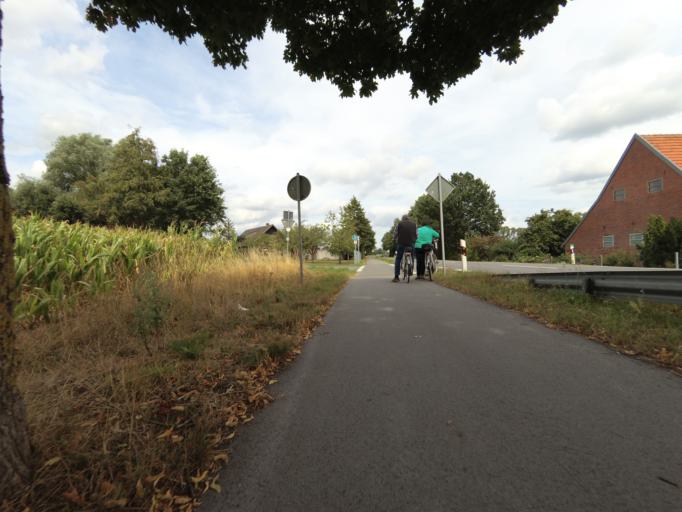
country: DE
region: North Rhine-Westphalia
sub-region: Regierungsbezirk Munster
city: Ahaus
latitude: 52.1305
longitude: 7.0055
